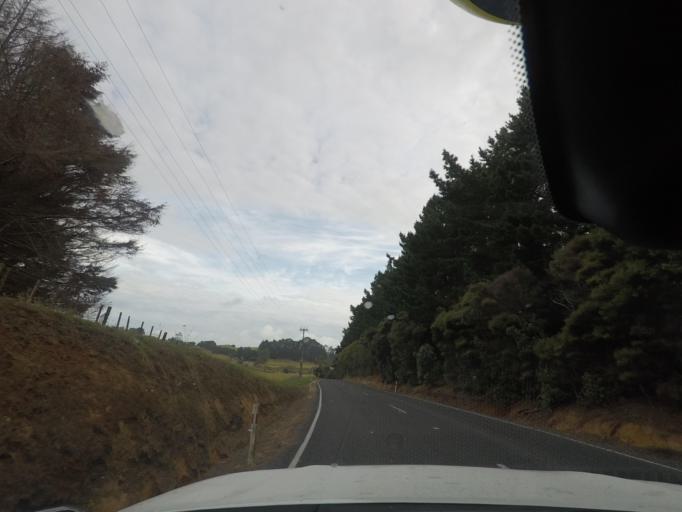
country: NZ
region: Auckland
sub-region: Auckland
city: Parakai
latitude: -36.5360
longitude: 174.2926
